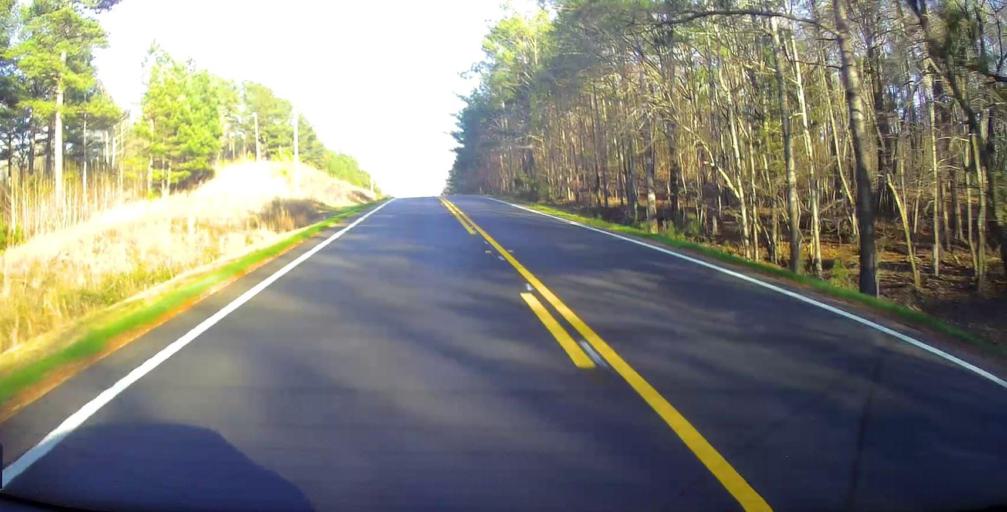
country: US
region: Georgia
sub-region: Harris County
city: Hamilton
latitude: 32.7472
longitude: -84.9928
